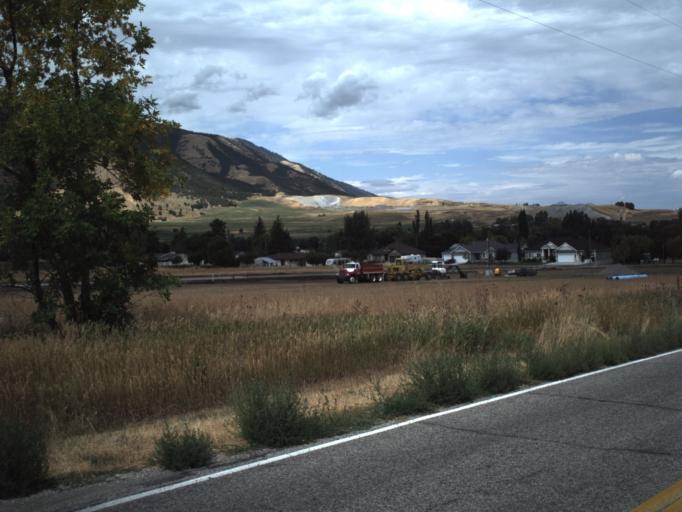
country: US
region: Utah
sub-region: Cache County
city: Wellsville
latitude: 41.6199
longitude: -111.9350
